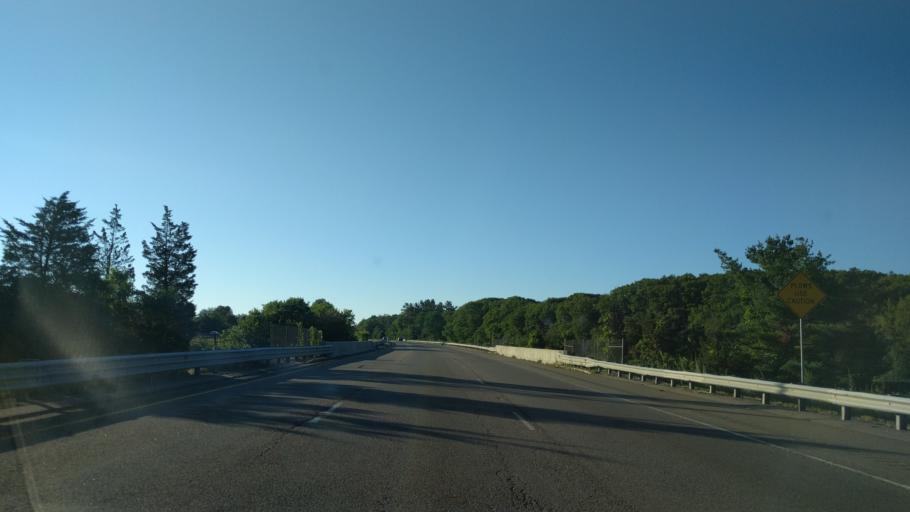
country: US
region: Massachusetts
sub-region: Norfolk County
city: Franklin
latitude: 42.0651
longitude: -71.4021
